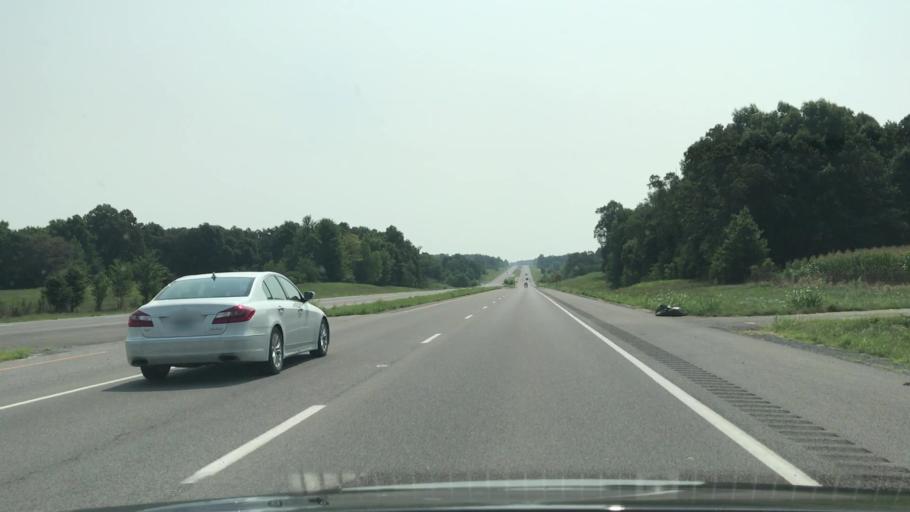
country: US
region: Kentucky
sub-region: Graves County
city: Mayfield
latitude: 36.6704
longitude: -88.5016
